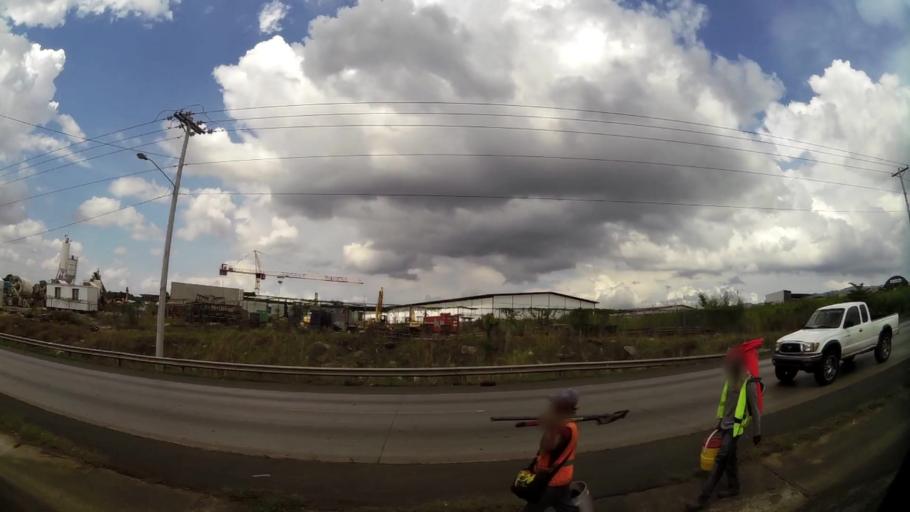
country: PA
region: Panama
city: Tocumen
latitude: 9.0879
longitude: -79.3967
